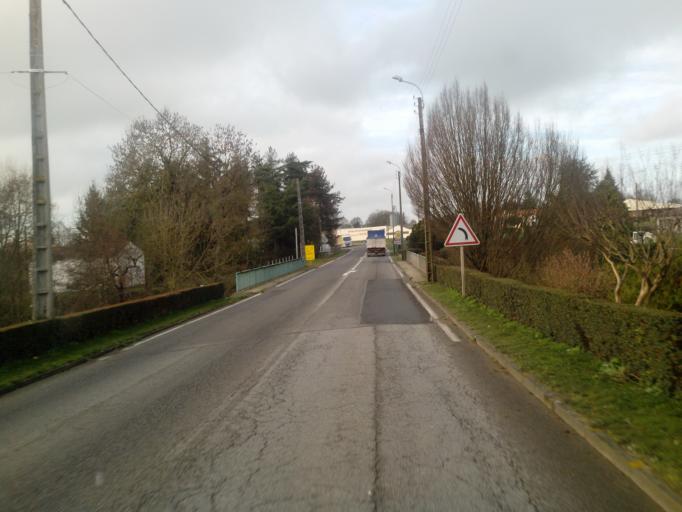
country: FR
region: Poitou-Charentes
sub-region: Departement des Deux-Sevres
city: Chiche
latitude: 46.7983
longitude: -0.3610
